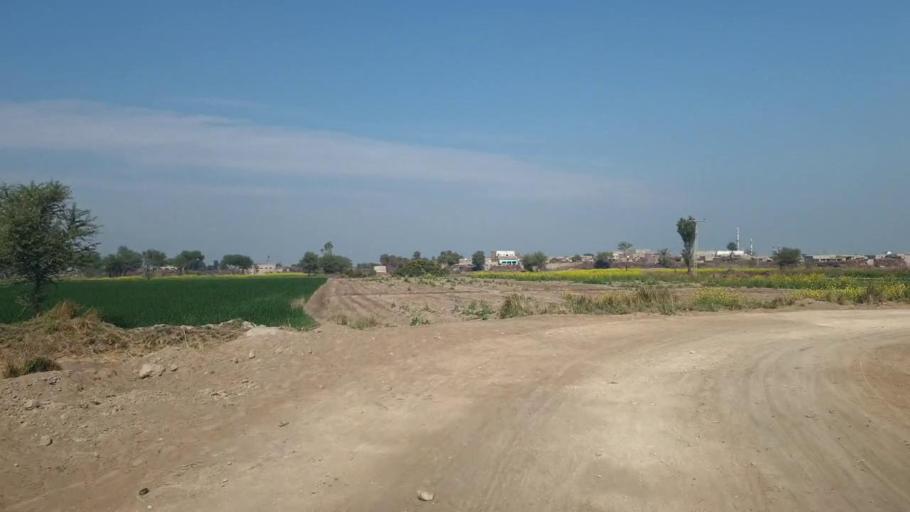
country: PK
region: Sindh
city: Shahdadpur
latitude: 25.9974
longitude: 68.5362
